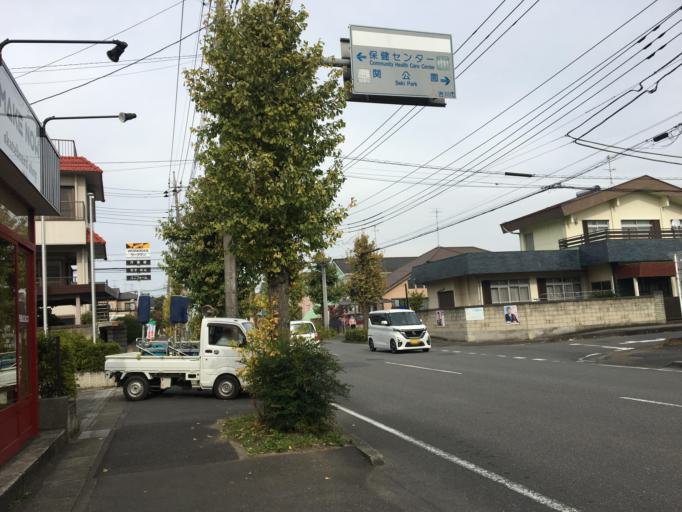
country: JP
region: Saitama
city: Yoshikawa
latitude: 35.8908
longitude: 139.8428
